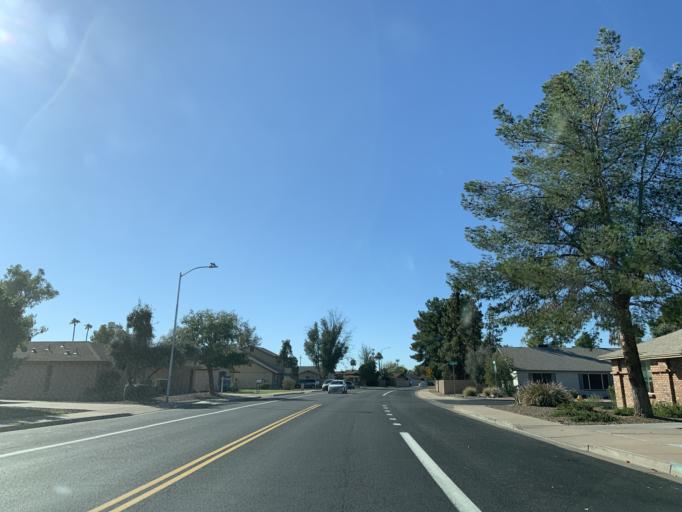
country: US
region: Arizona
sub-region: Maricopa County
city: San Carlos
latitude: 33.3677
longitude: -111.8622
